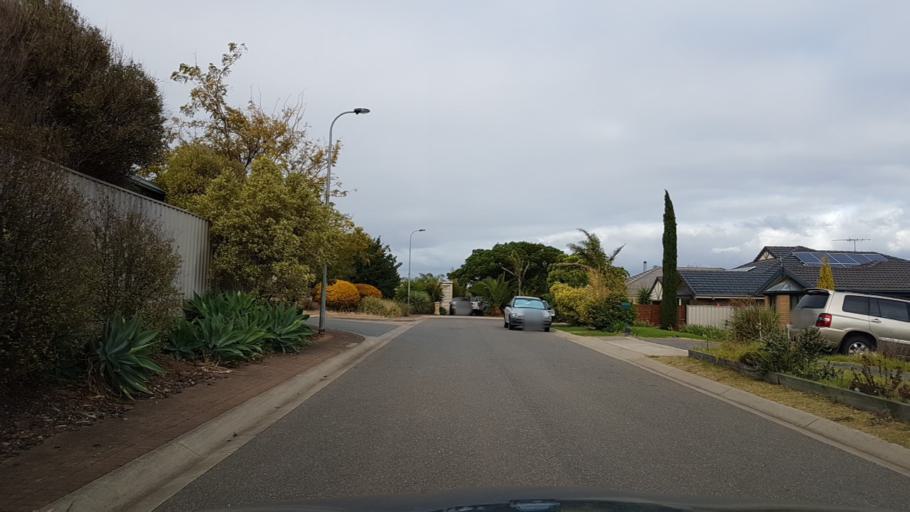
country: AU
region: South Australia
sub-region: Onkaparinga
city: Moana
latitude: -35.2090
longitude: 138.4889
